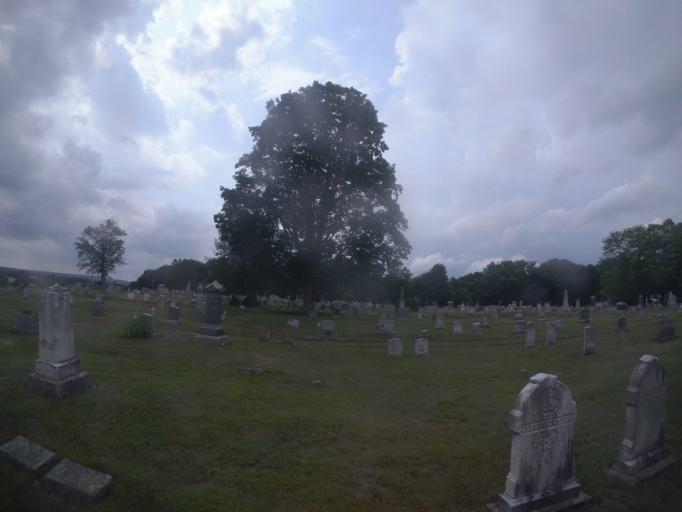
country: US
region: Maine
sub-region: Cumberland County
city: New Gloucester
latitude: 43.8853
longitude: -70.3329
